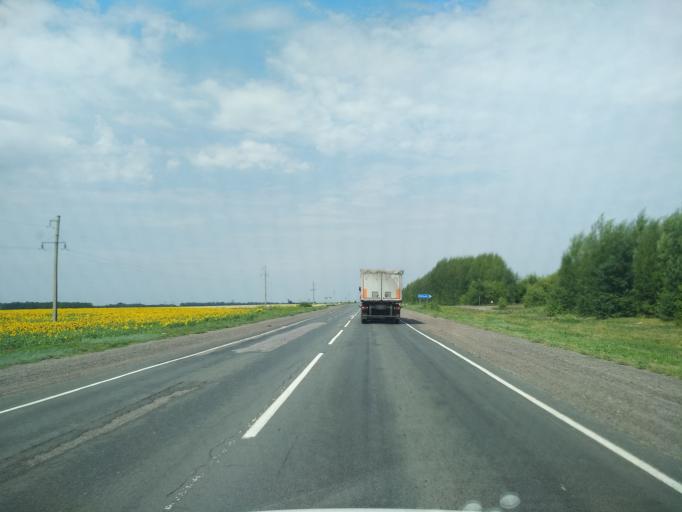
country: RU
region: Voronezj
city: Orlovo
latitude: 51.6768
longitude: 39.6956
